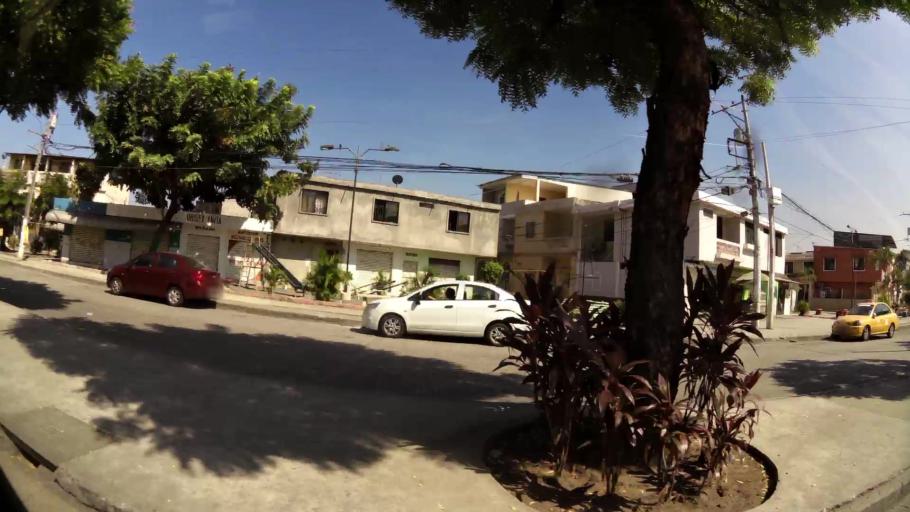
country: EC
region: Guayas
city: Eloy Alfaro
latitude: -2.1238
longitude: -79.8899
